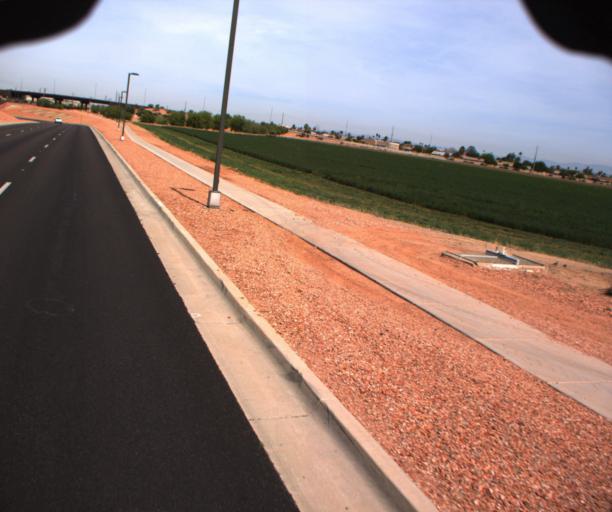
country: US
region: Arizona
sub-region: Maricopa County
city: Peoria
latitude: 33.5632
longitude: -112.2137
